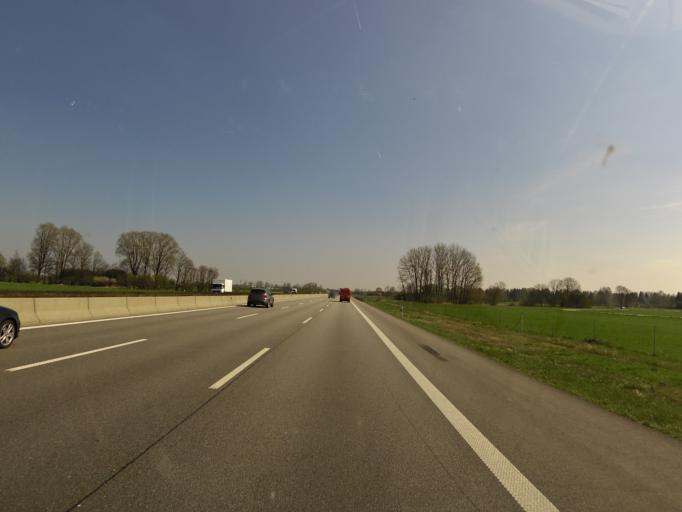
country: DE
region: Bavaria
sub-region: Upper Bavaria
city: Bergkirchen
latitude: 48.2463
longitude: 11.3229
